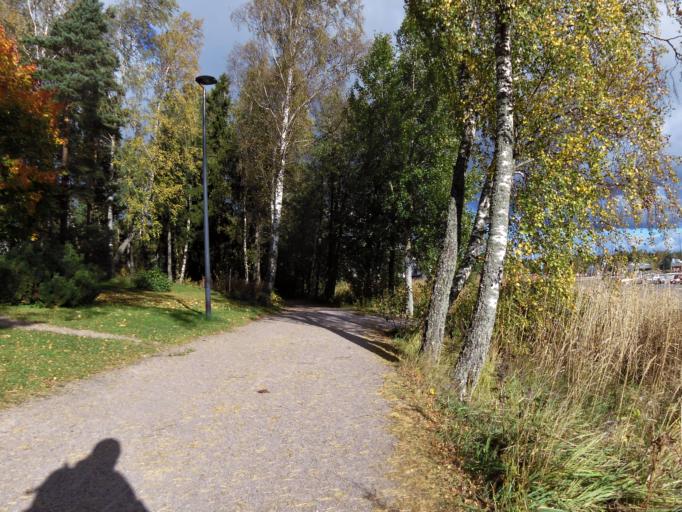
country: FI
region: Uusimaa
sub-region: Helsinki
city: Koukkuniemi
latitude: 60.1465
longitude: 24.7529
